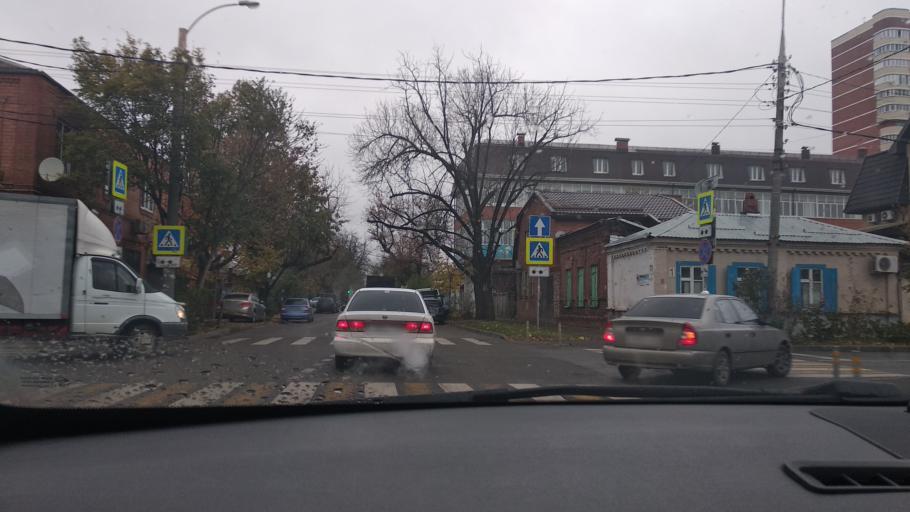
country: RU
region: Krasnodarskiy
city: Krasnodar
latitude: 45.0279
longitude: 38.9827
